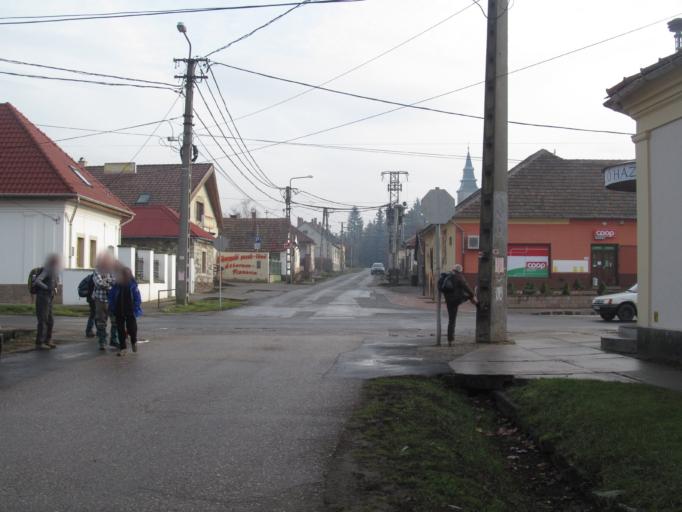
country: HU
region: Borsod-Abauj-Zemplen
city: Bogacs
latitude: 47.9051
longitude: 20.5316
